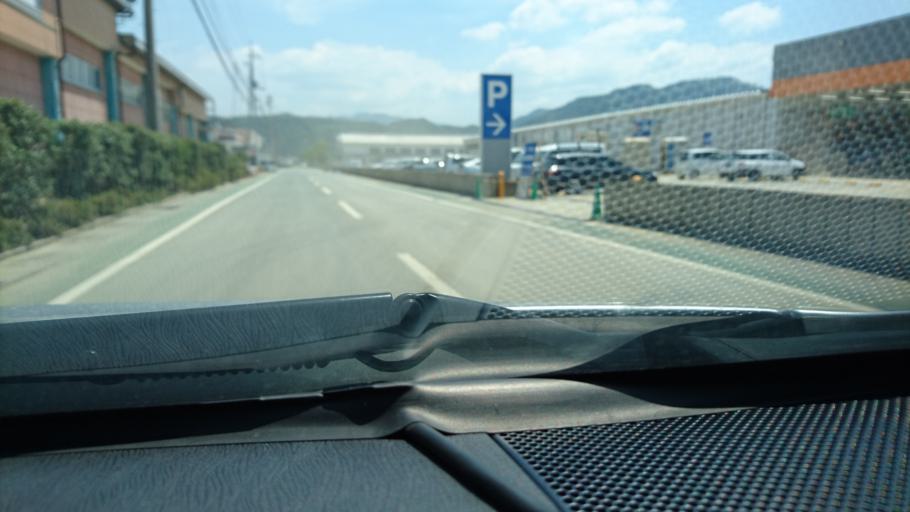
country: JP
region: Ehime
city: Ozu
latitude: 33.5302
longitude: 132.5721
